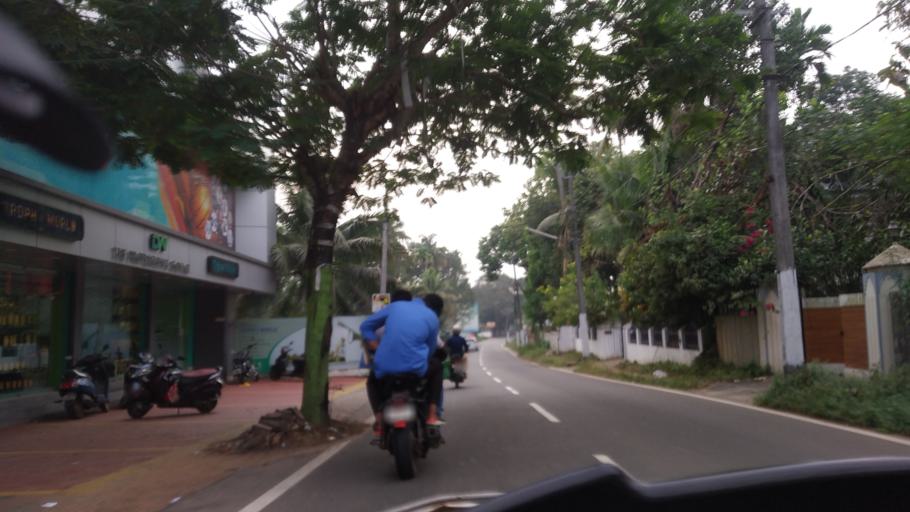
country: IN
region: Kerala
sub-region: Ernakulam
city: Elur
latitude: 10.1499
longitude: 76.2620
